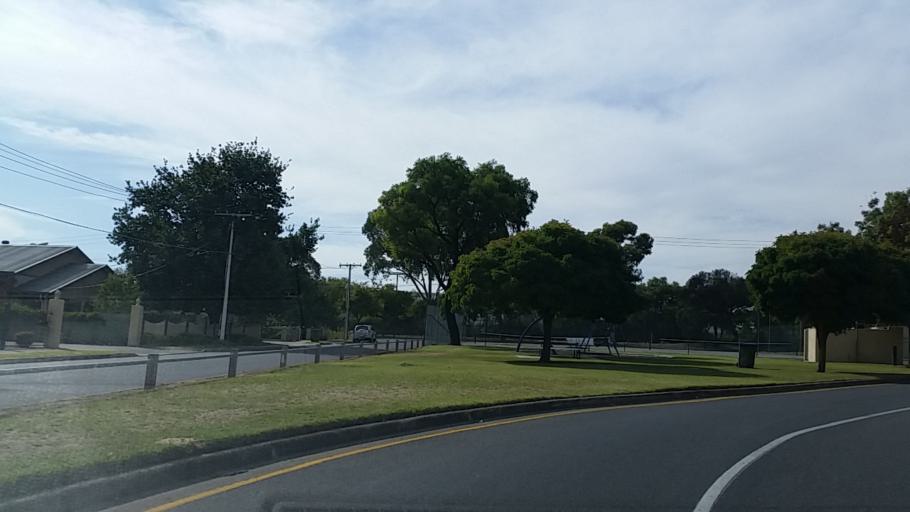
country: AU
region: South Australia
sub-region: Charles Sturt
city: Woodville West
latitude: -34.8770
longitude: 138.5341
